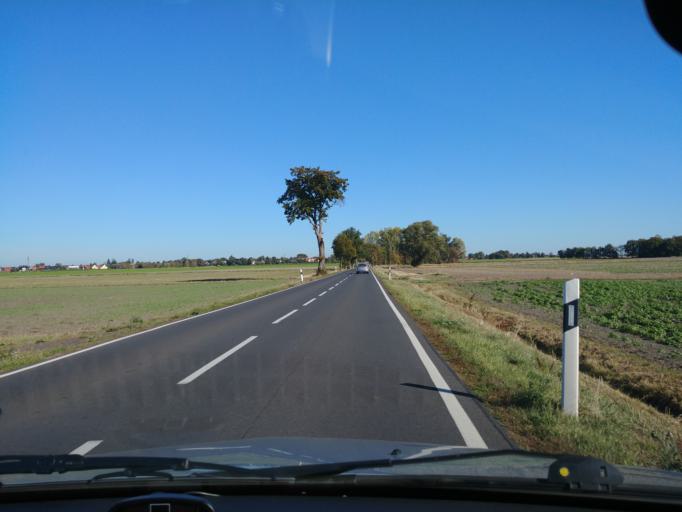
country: DE
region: Lower Saxony
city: Leiferde
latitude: 52.4255
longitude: 10.4273
